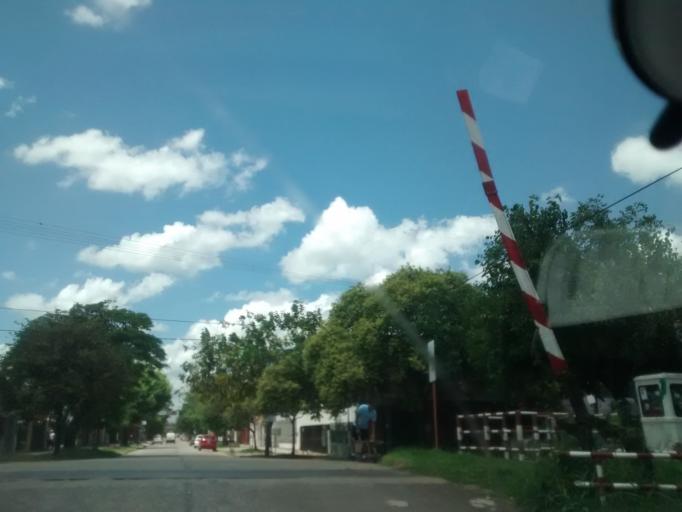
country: AR
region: Chaco
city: Resistencia
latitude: -27.4559
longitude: -58.9901
